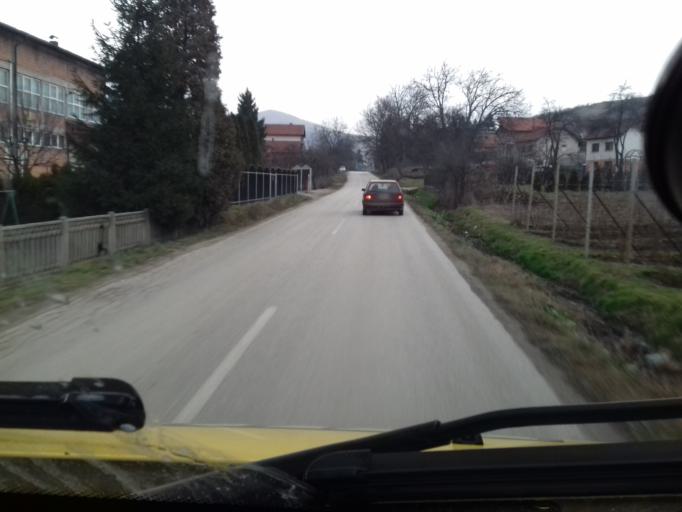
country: BA
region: Federation of Bosnia and Herzegovina
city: Zenica
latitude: 44.1818
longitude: 17.9598
